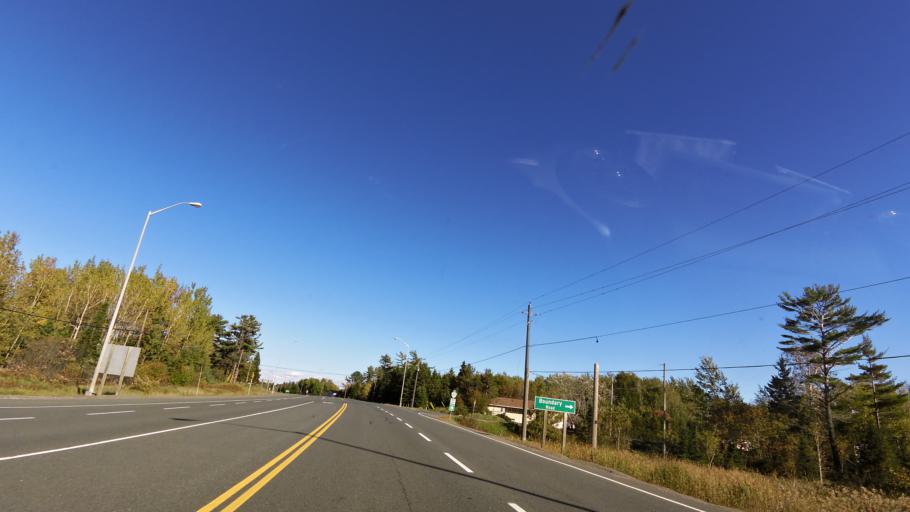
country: CA
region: Ontario
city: Thessalon
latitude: 46.2654
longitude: -83.5463
